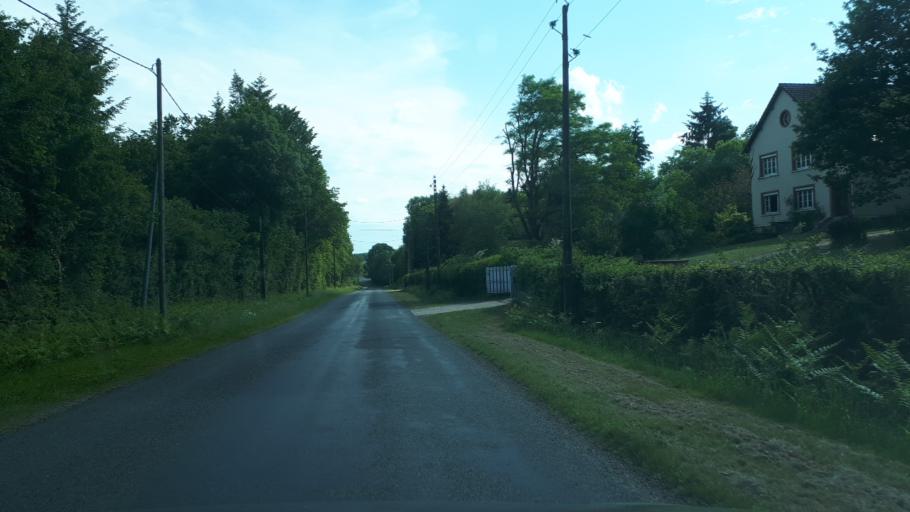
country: FR
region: Centre
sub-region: Departement du Cher
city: Henrichemont
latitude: 47.3766
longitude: 2.5954
